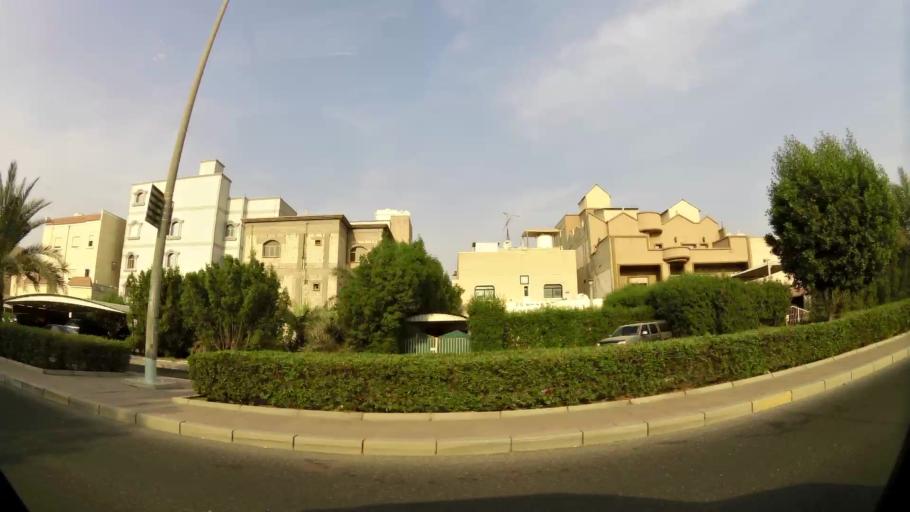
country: KW
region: Mubarak al Kabir
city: Mubarak al Kabir
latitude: 29.2149
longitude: 48.0646
